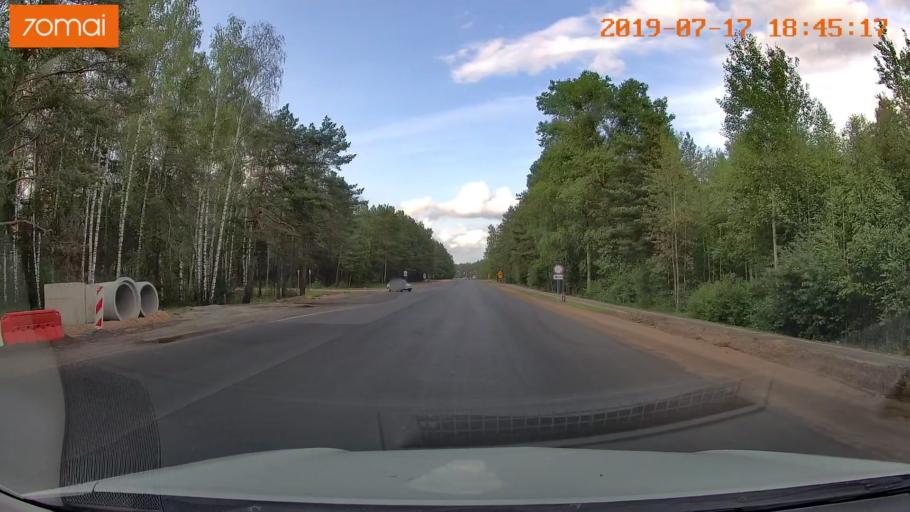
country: BY
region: Mogilev
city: Asipovichy
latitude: 53.3236
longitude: 28.6531
